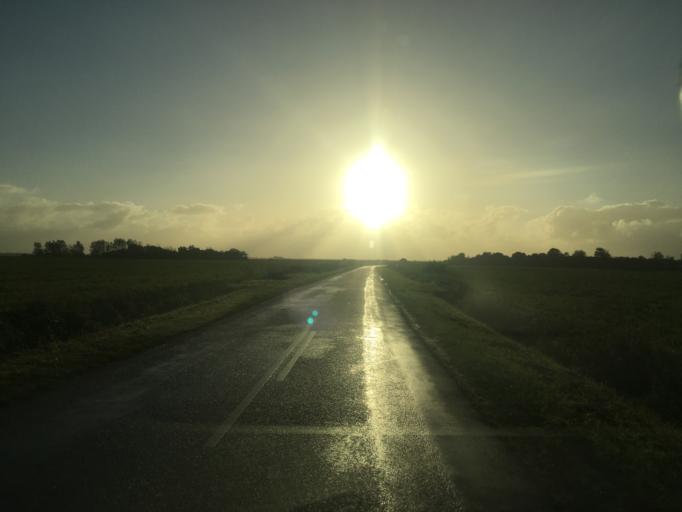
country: DE
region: Schleswig-Holstein
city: Aventoft
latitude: 54.9470
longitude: 8.7869
